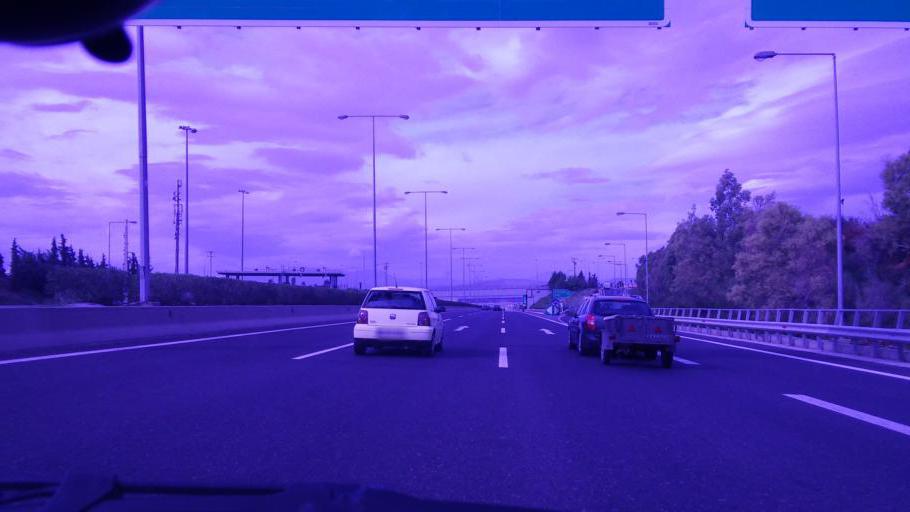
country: GR
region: Attica
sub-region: Nomarchia Dytikis Attikis
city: Aspropyrgos
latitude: 38.0892
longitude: 23.6245
